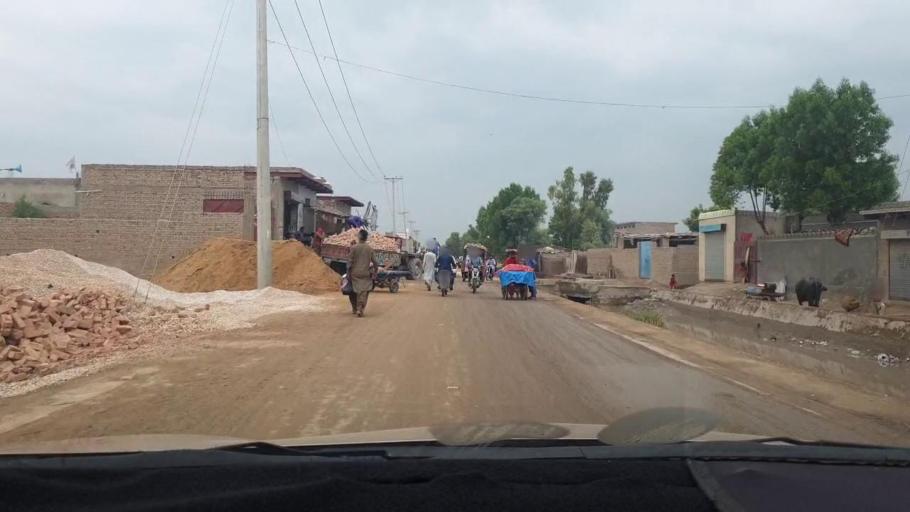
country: PK
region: Sindh
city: Larkana
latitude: 27.5821
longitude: 68.2159
